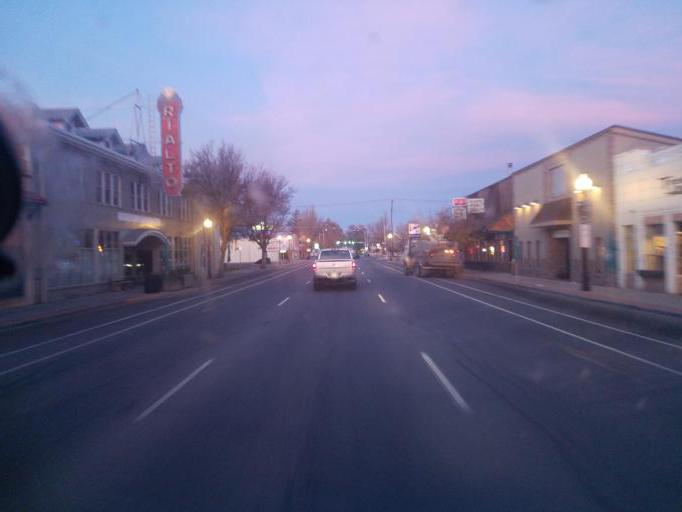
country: US
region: Colorado
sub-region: Alamosa County
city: Alamosa
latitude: 37.4682
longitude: -105.8675
